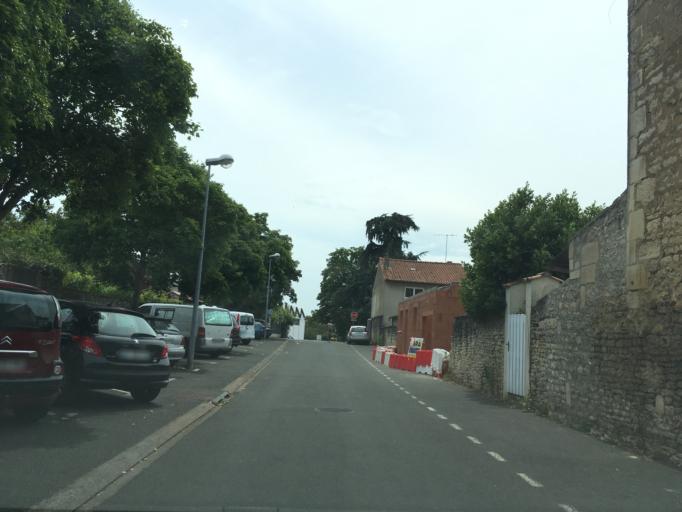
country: FR
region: Poitou-Charentes
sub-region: Departement des Deux-Sevres
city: Niort
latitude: 46.3220
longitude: -0.4758
